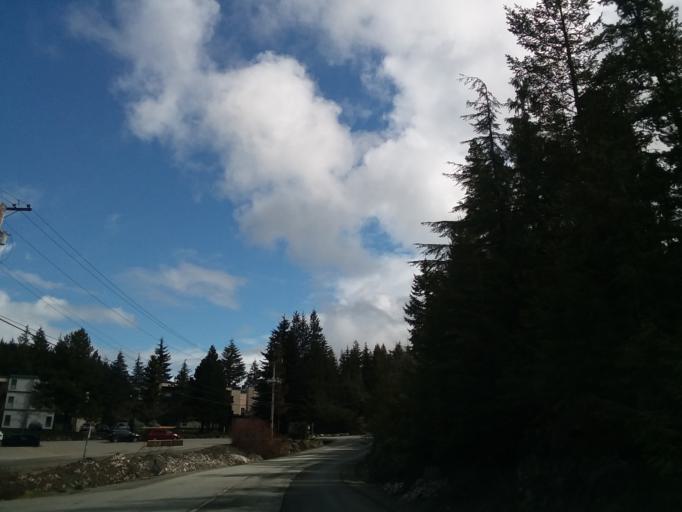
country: CA
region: British Columbia
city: Whistler
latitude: 50.0914
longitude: -123.0111
